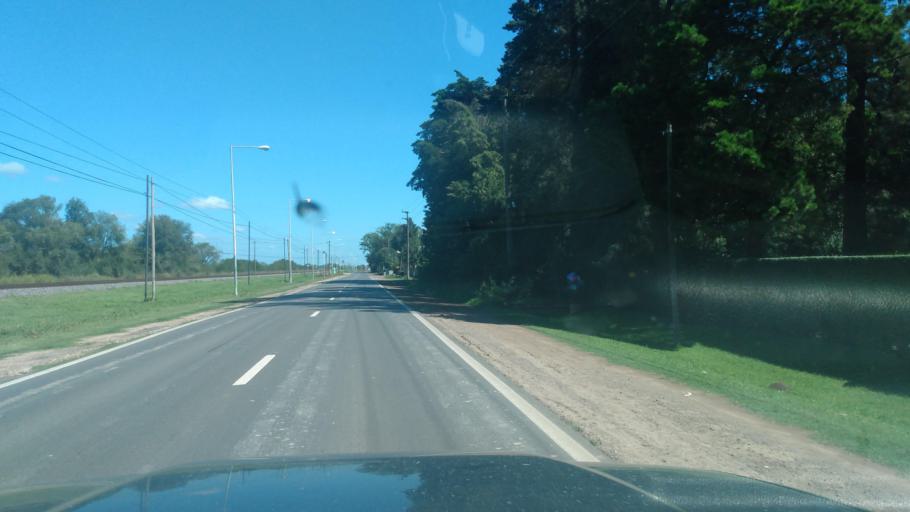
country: AR
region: Buenos Aires
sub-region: Partido de General Rodriguez
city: General Rodriguez
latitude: -34.5939
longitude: -59.0159
